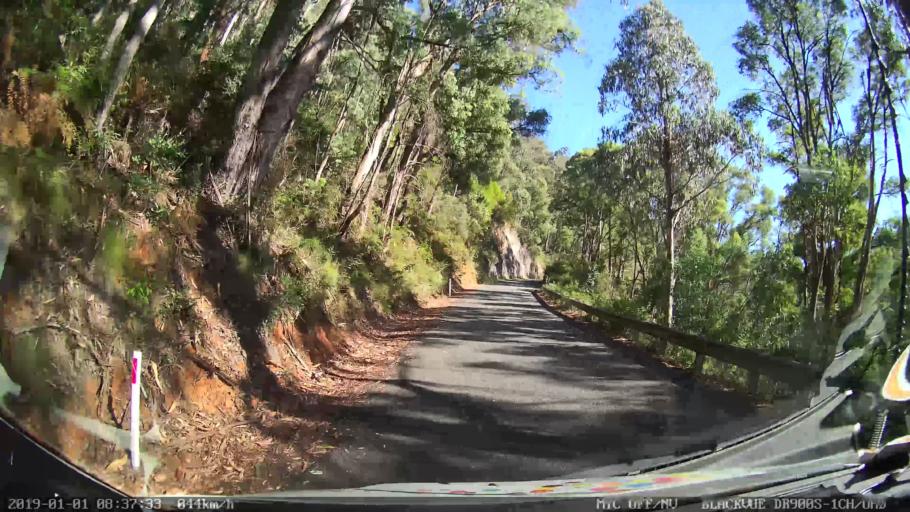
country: AU
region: New South Wales
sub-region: Snowy River
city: Jindabyne
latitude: -36.3377
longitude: 148.1963
